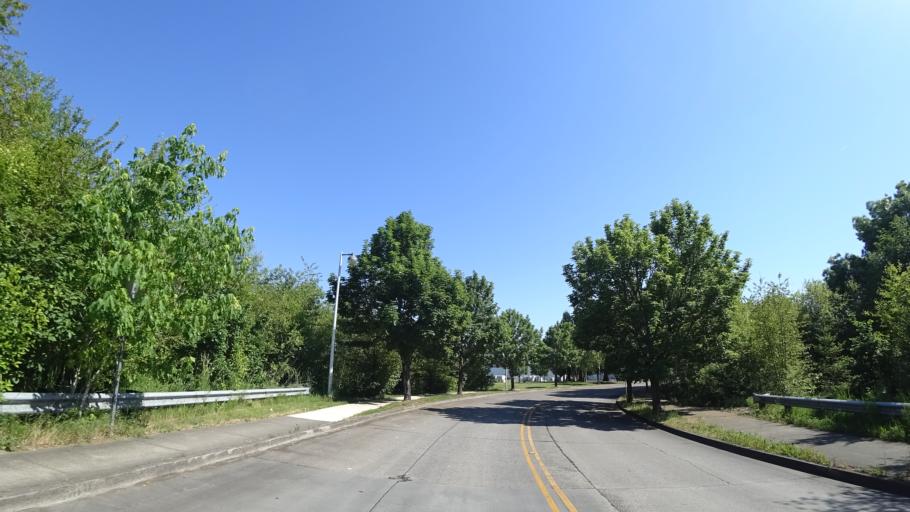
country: US
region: Oregon
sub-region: Washington County
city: Beaverton
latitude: 45.4929
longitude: -122.8320
